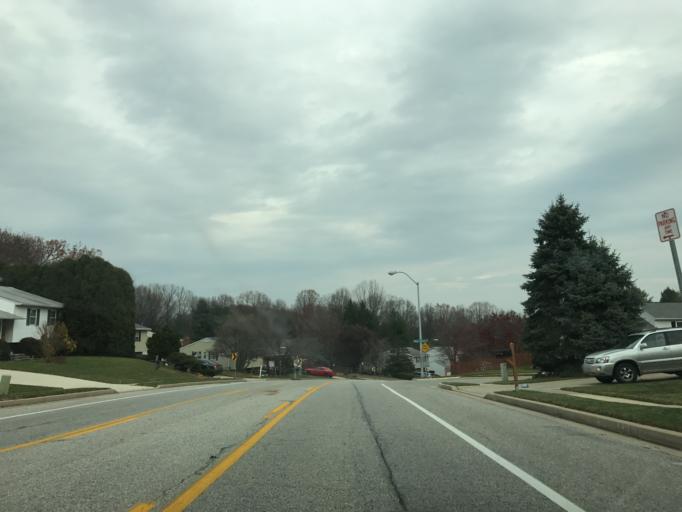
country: US
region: Maryland
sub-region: Baltimore County
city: Carney
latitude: 39.4093
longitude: -76.5365
